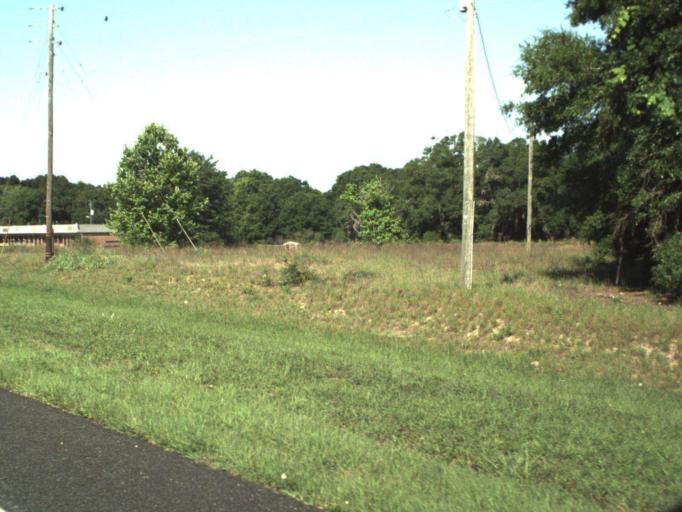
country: US
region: Florida
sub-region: Marion County
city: Citra
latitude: 29.3986
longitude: -82.1156
